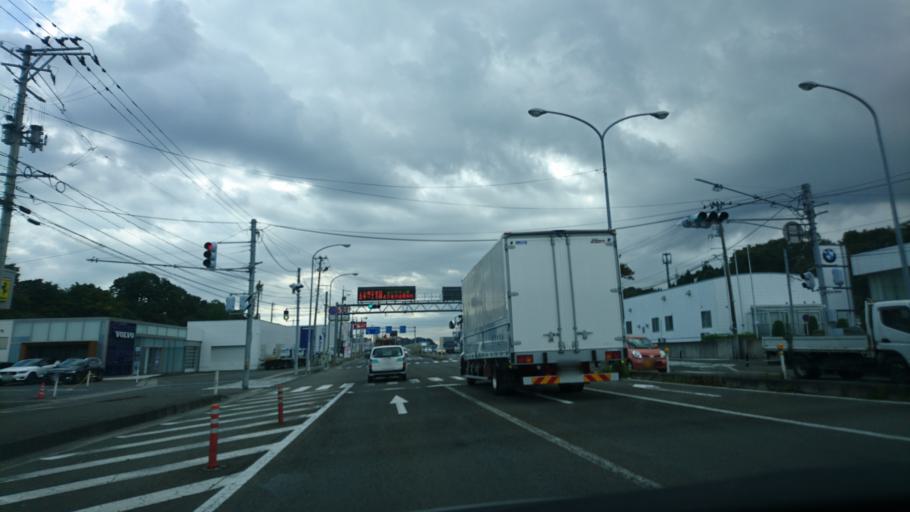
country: JP
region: Miyagi
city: Tomiya
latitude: 38.3410
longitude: 140.8829
